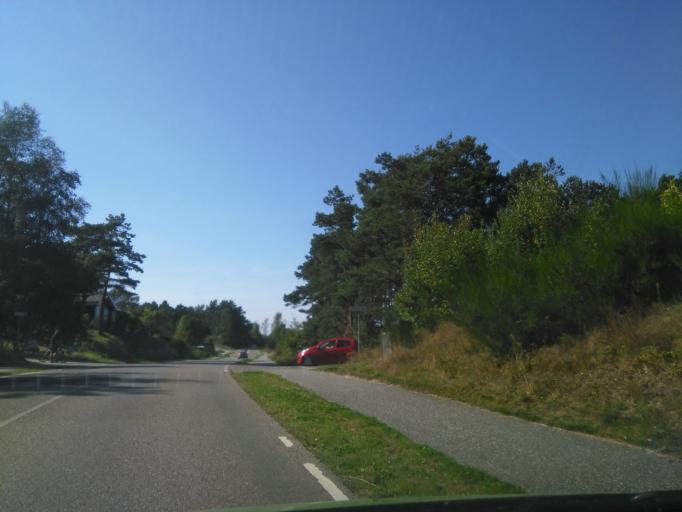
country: DK
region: Central Jutland
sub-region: Syddjurs Kommune
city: Ebeltoft
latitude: 56.2005
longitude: 10.7002
